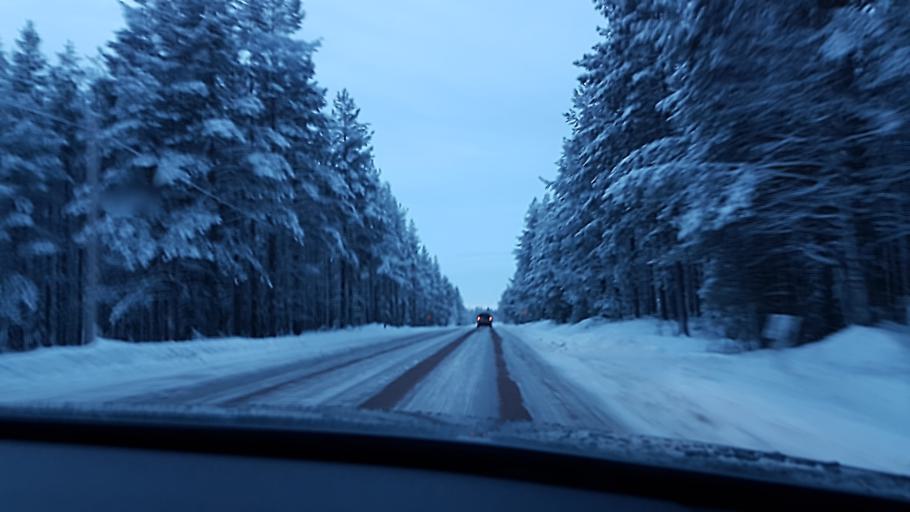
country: SE
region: Jaemtland
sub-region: Harjedalens Kommun
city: Sveg
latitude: 62.0584
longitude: 14.5700
